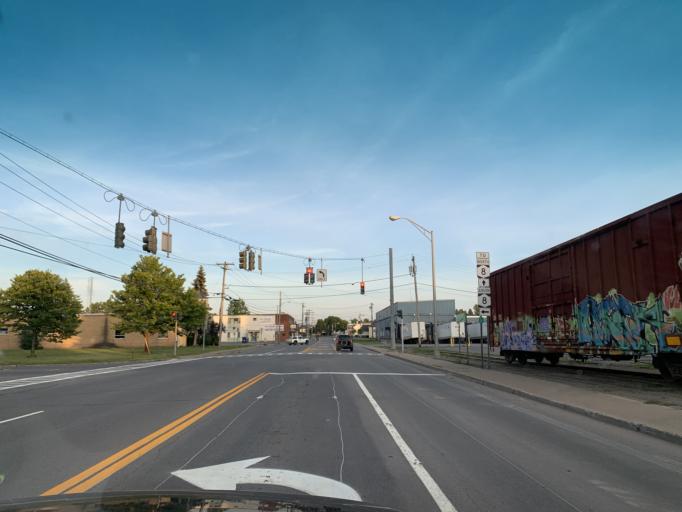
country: US
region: New York
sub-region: Oneida County
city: New Hartford
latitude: 43.0770
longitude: -75.2905
